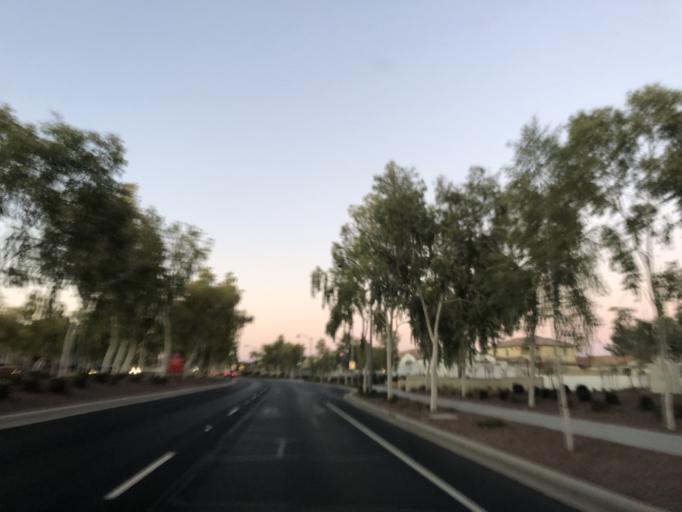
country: US
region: Arizona
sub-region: Maricopa County
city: Citrus Park
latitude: 33.4729
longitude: -112.5037
